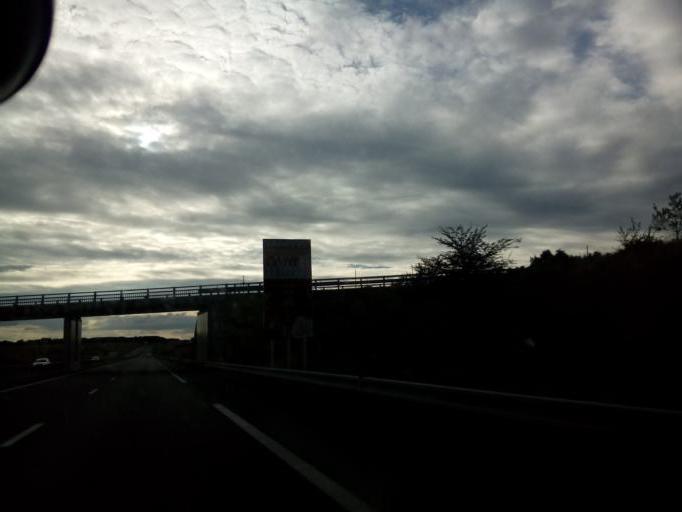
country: FR
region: Centre
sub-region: Departement d'Indre-et-Loire
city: Monts
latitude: 47.3070
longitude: 0.6512
